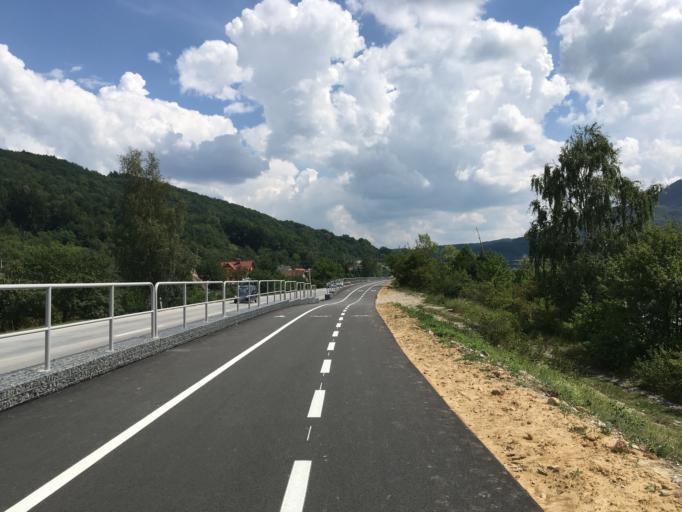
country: SK
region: Nitriansky
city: Puchov
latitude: 49.1378
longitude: 18.3562
